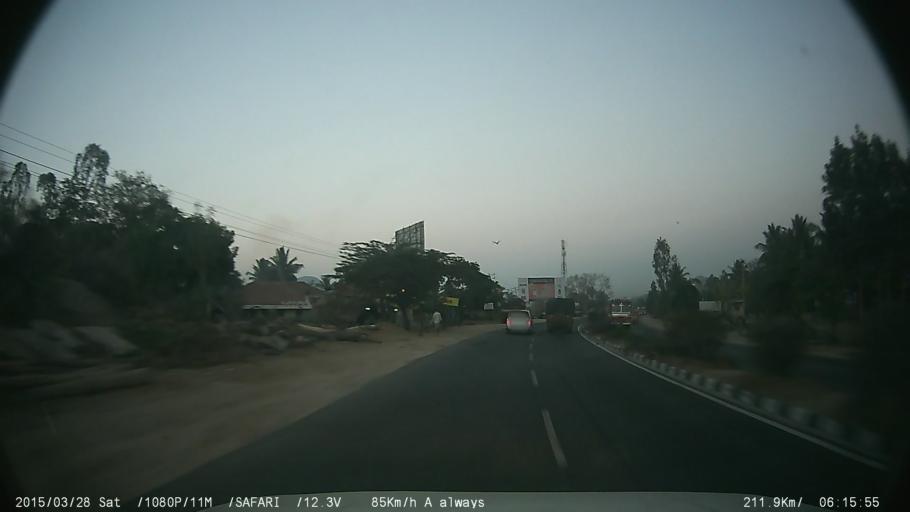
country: IN
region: Karnataka
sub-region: Ramanagara
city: Ramanagaram
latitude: 12.7595
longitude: 77.3258
